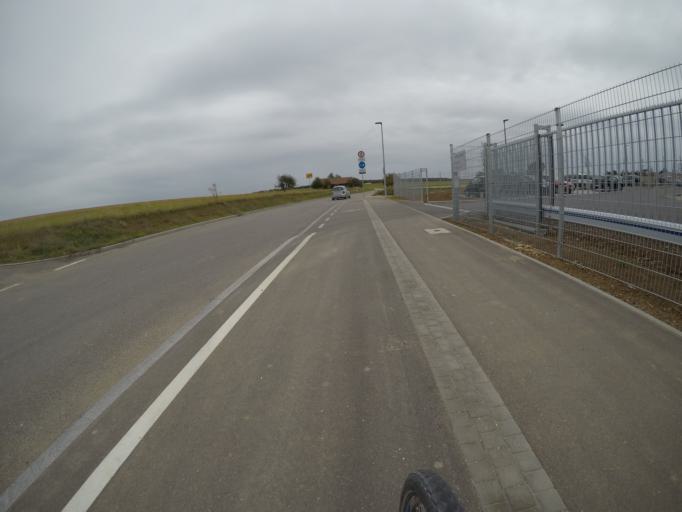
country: DE
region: Baden-Wuerttemberg
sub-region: Regierungsbezirk Stuttgart
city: Eberdingen
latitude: 48.8487
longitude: 8.9856
